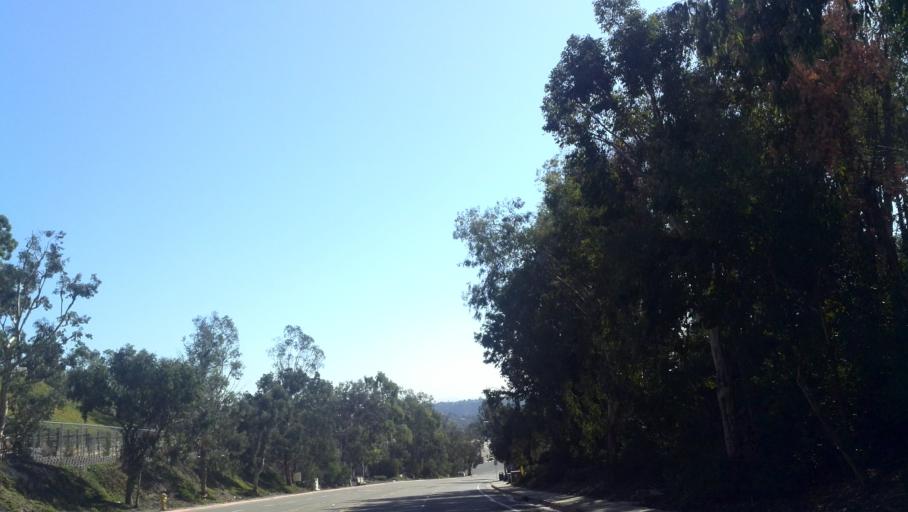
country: US
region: California
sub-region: San Diego County
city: San Diego
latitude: 32.8120
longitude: -117.1201
